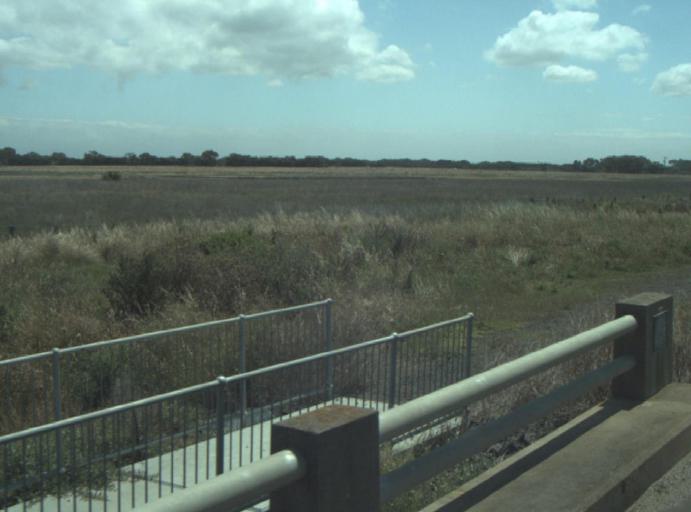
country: AU
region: Victoria
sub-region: Greater Geelong
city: Breakwater
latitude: -38.2869
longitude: 144.3970
